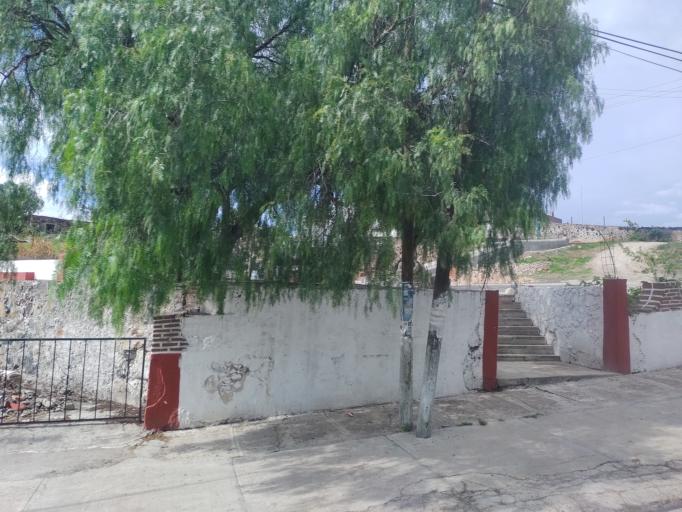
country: MX
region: Mexico
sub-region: Aculco
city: El Colorado
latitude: 20.1065
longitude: -99.7259
